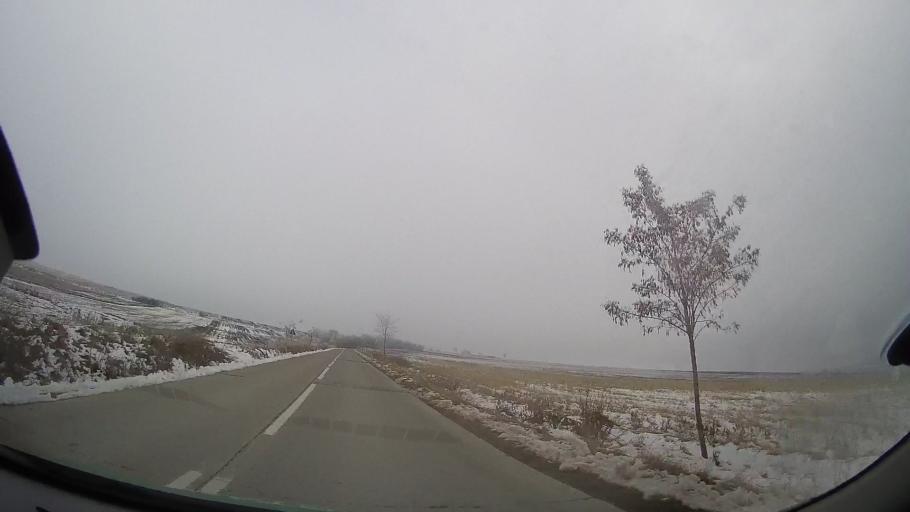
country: RO
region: Vaslui
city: Coroiesti
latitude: 46.2138
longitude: 27.4749
